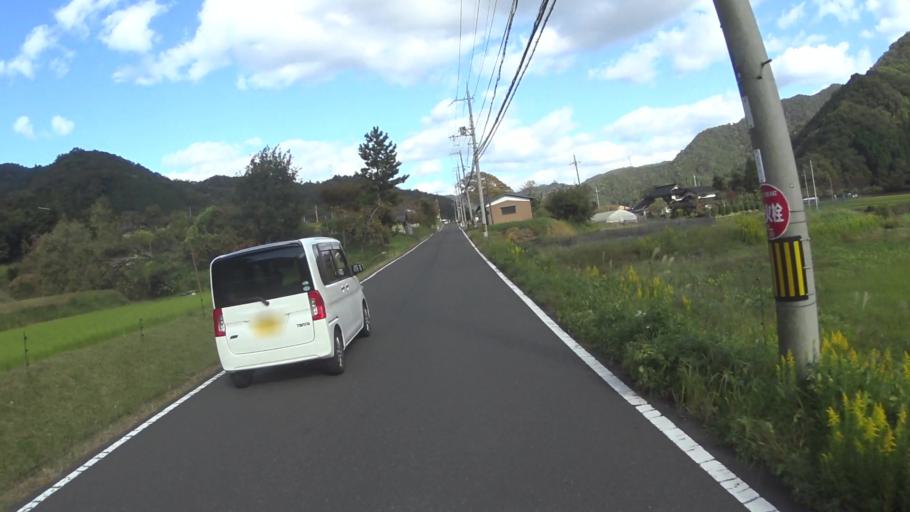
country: JP
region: Kyoto
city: Maizuru
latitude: 35.5238
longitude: 135.4079
